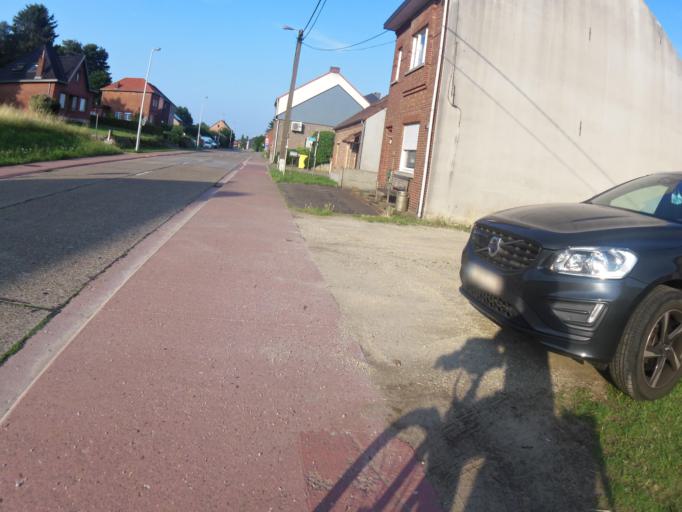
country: BE
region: Flanders
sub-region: Provincie Vlaams-Brabant
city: Scherpenheuvel-Zichem
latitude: 51.0156
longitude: 4.9404
